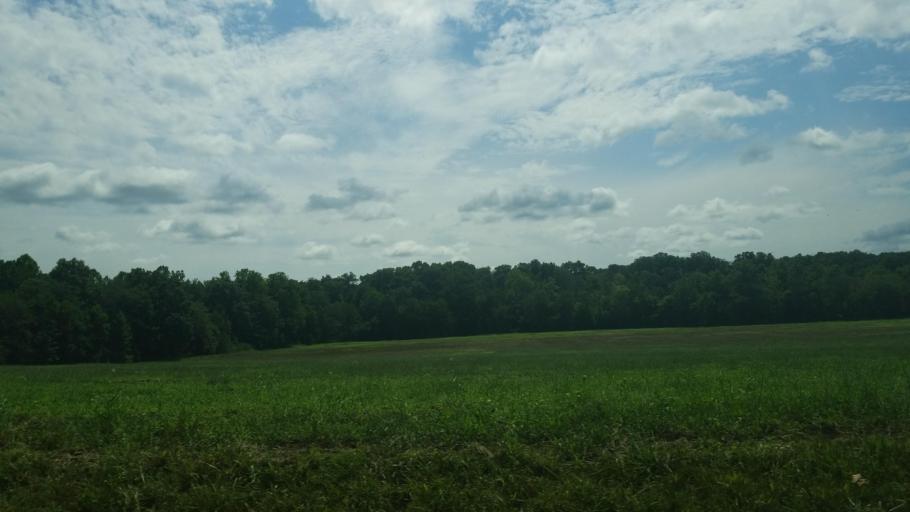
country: US
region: Illinois
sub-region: Saline County
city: Carrier Mills
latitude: 37.7988
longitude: -88.7405
